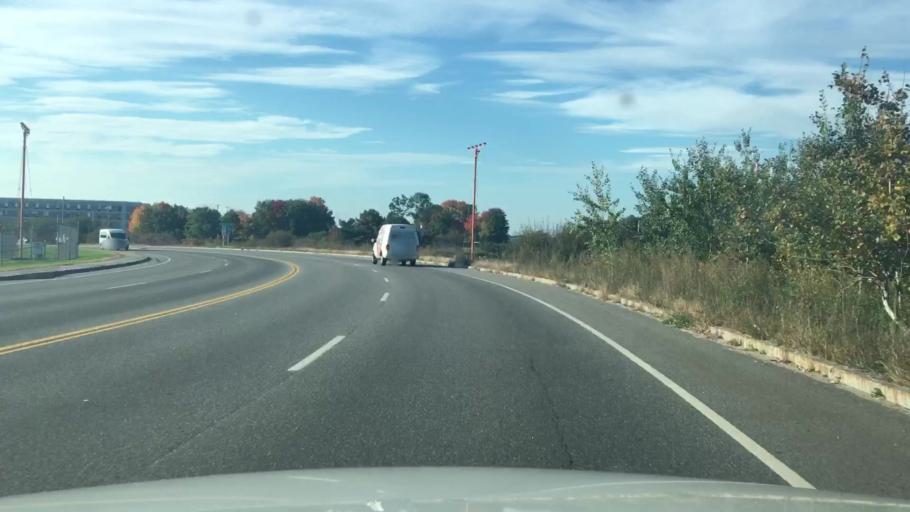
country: US
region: Maine
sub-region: Cumberland County
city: South Portland Gardens
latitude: 43.6467
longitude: -70.3305
